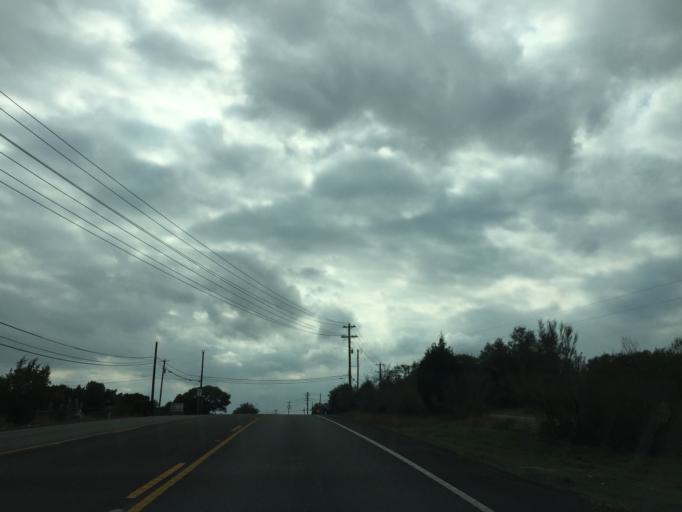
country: US
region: Texas
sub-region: Travis County
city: Shady Hollow
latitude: 30.1635
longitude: -97.9502
